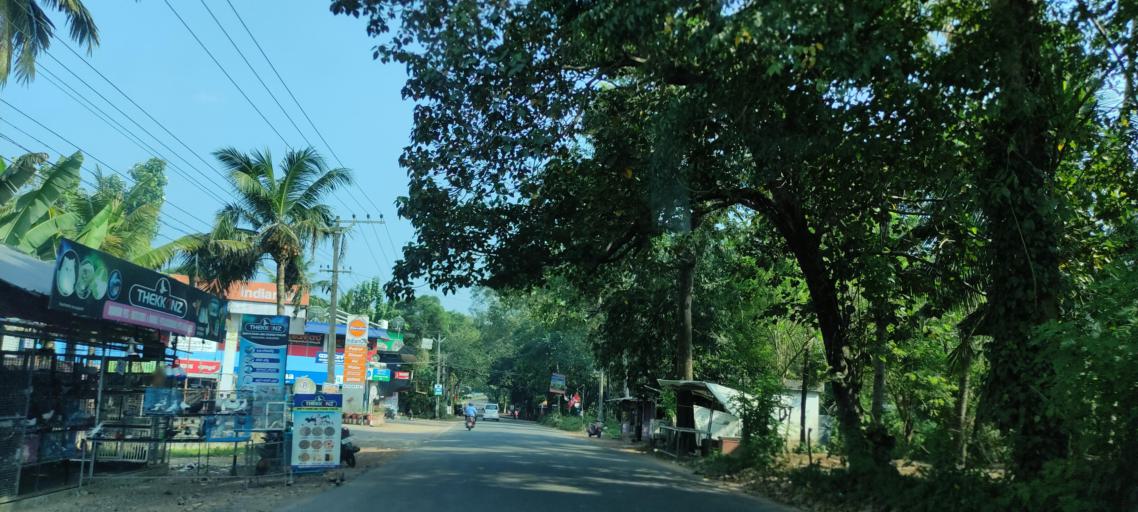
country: IN
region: Kerala
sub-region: Kollam
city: Panmana
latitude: 9.0514
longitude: 76.5629
